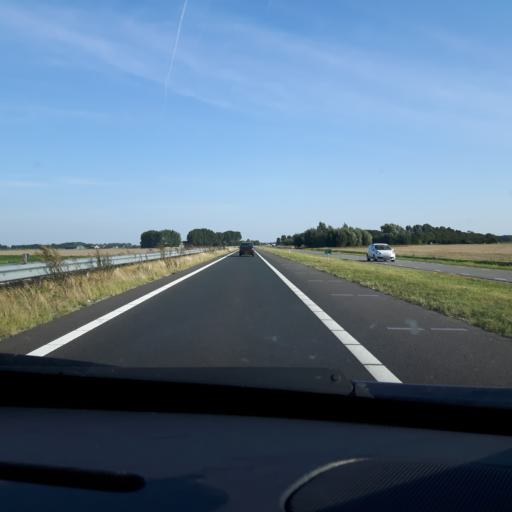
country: BE
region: Flanders
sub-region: Provincie Oost-Vlaanderen
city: Sint-Laureins
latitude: 51.3333
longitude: 3.5808
